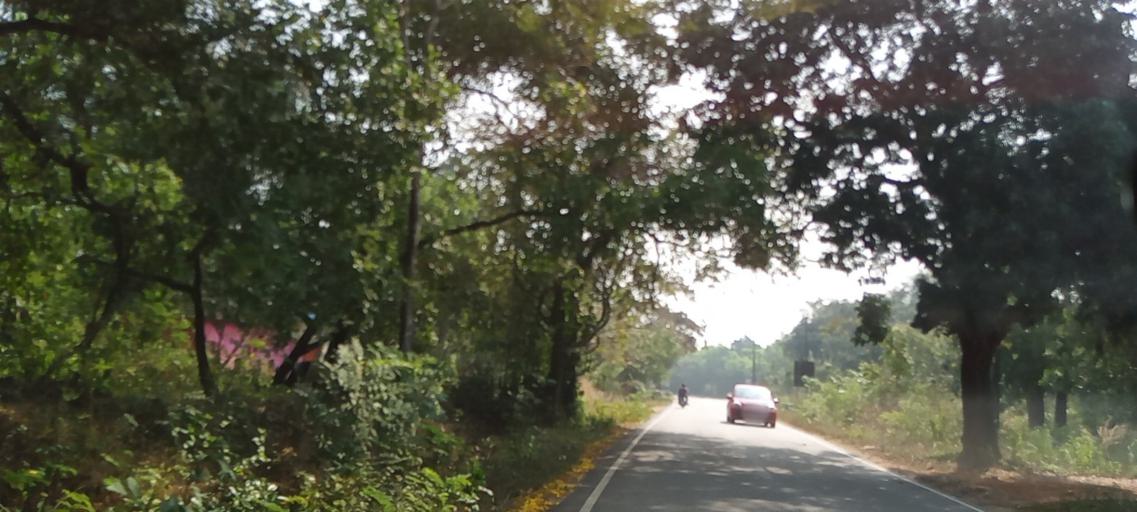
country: IN
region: Karnataka
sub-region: Udupi
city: Coondapoor
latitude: 13.5118
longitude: 74.7801
